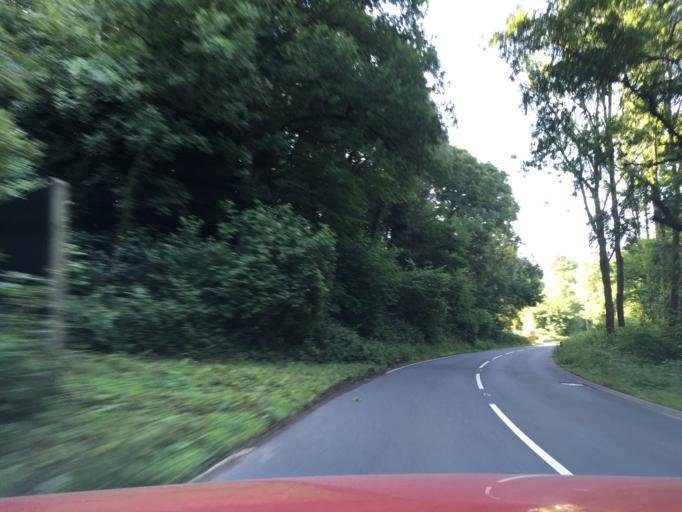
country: GB
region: England
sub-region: Gloucestershire
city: Lydney
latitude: 51.7387
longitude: -2.5377
